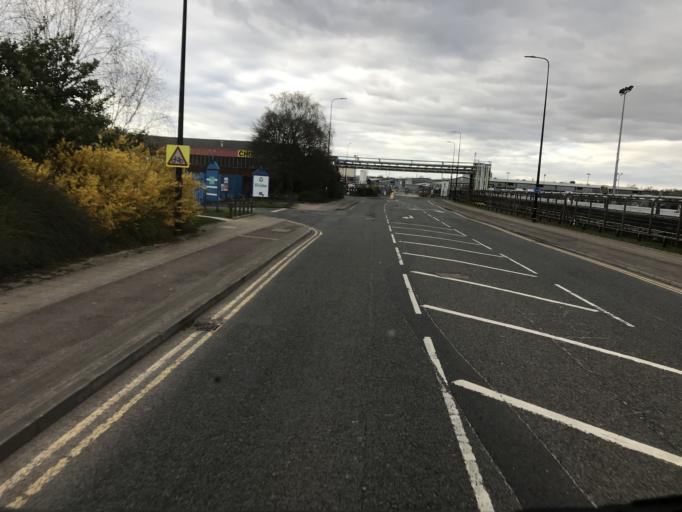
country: GB
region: England
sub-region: Trafford
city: Trafford Park
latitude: 53.4724
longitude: -2.3097
